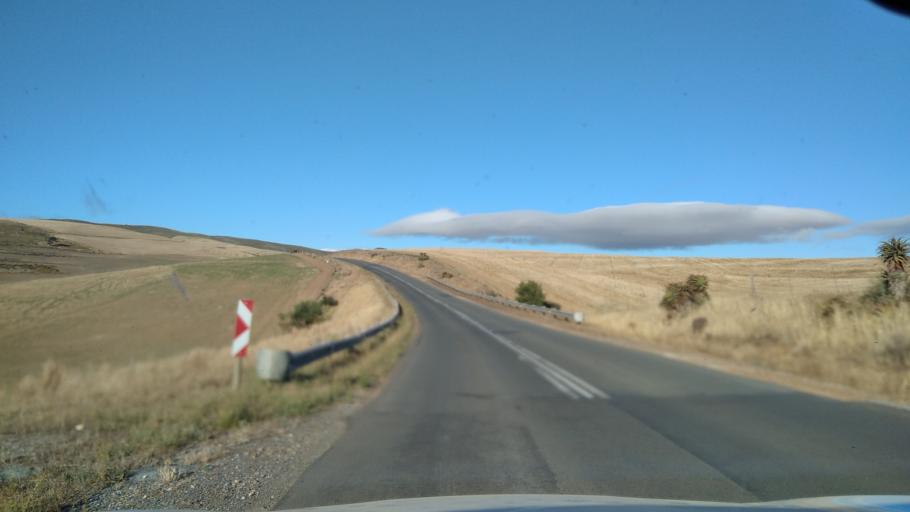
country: ZA
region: Western Cape
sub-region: Overberg District Municipality
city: Caledon
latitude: -34.1653
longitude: 19.2980
